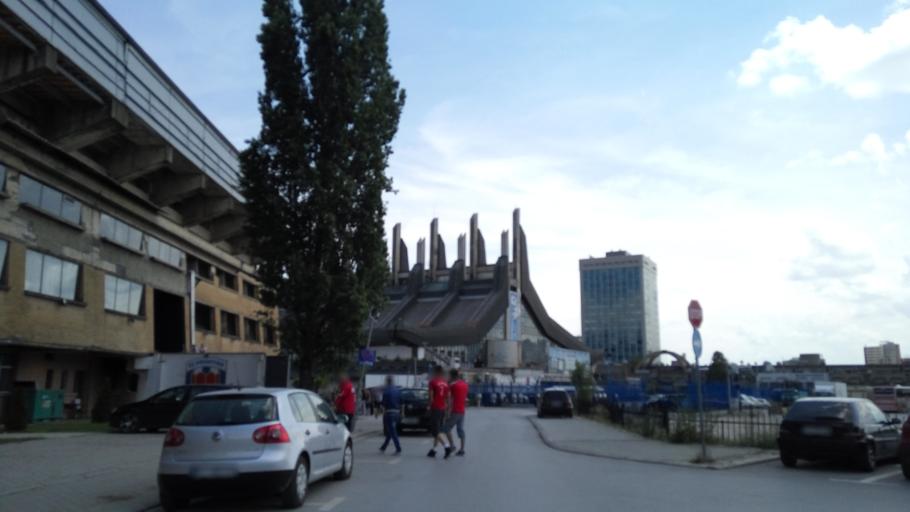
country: XK
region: Pristina
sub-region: Komuna e Prishtines
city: Pristina
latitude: 42.6628
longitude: 21.1558
